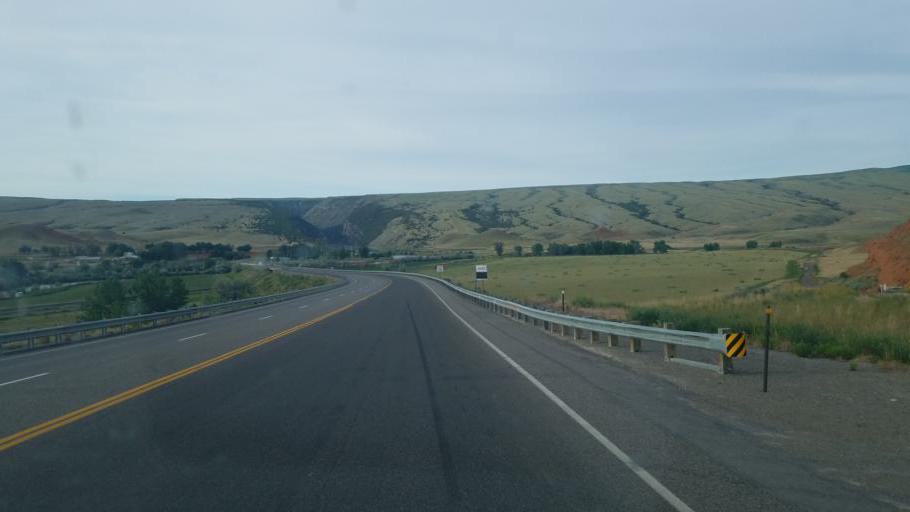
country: US
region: Wyoming
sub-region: Hot Springs County
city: Thermopolis
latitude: 43.5988
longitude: -108.2159
